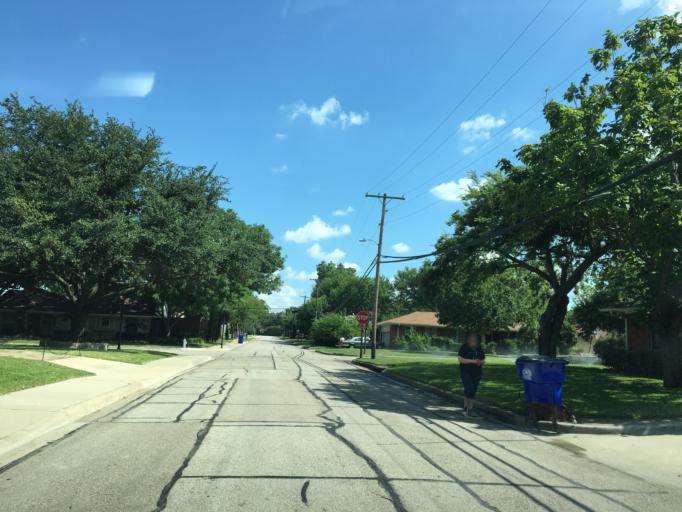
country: US
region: Texas
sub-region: Dallas County
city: Farmers Branch
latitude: 32.9214
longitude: -96.8792
